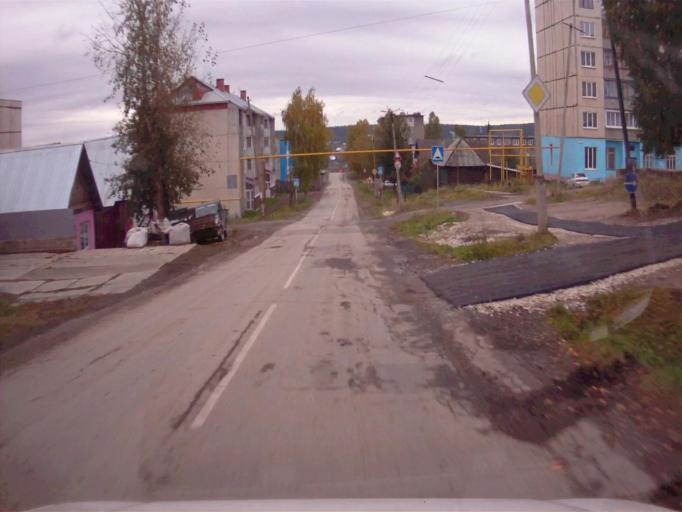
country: RU
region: Chelyabinsk
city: Nyazepetrovsk
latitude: 56.0568
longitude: 59.6071
